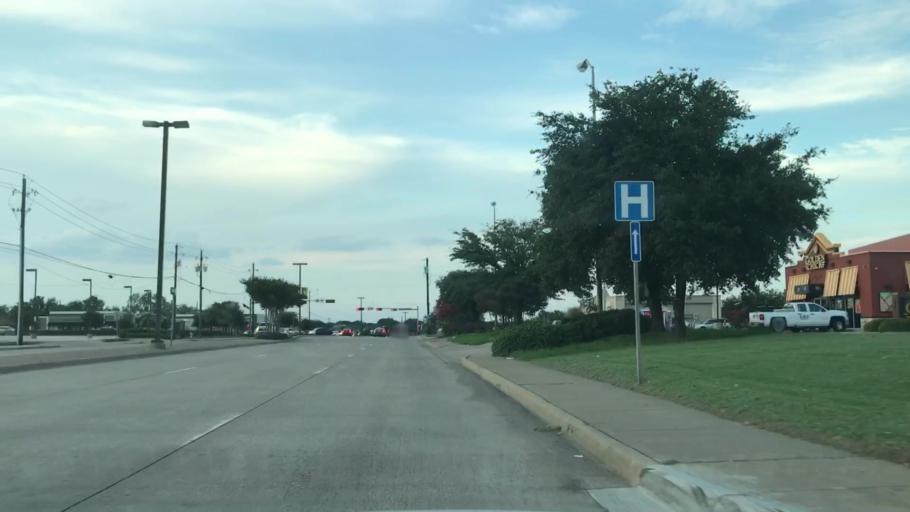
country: US
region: Texas
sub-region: Dallas County
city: Carrollton
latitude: 32.9985
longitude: -96.8866
